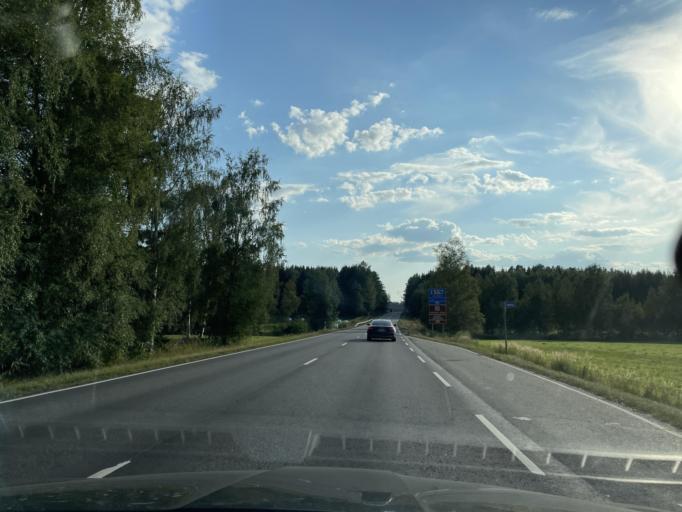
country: FI
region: Haeme
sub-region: Haemeenlinna
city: Tuulos
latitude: 61.1096
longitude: 24.8749
